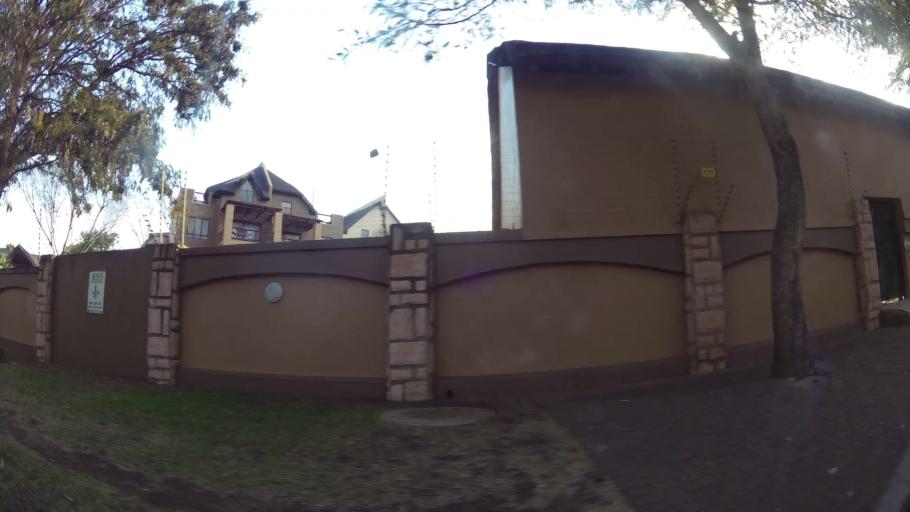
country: ZA
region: Gauteng
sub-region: City of Johannesburg Metropolitan Municipality
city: Diepsloot
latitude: -26.0172
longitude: 28.0168
